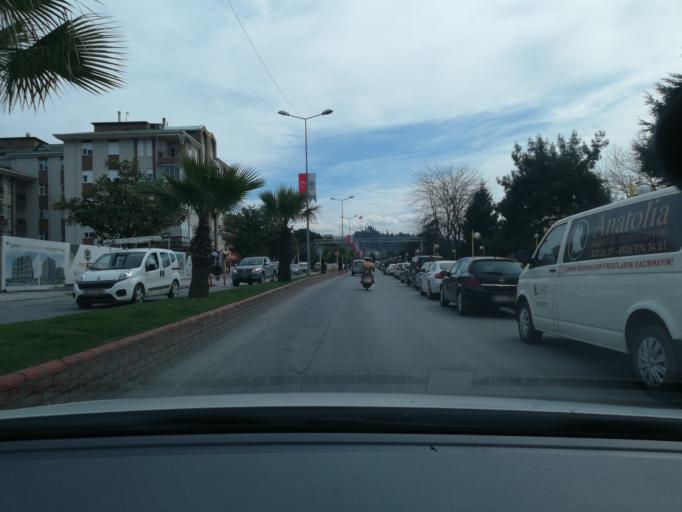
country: TR
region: Zonguldak
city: Eregli
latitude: 41.2841
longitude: 31.4134
